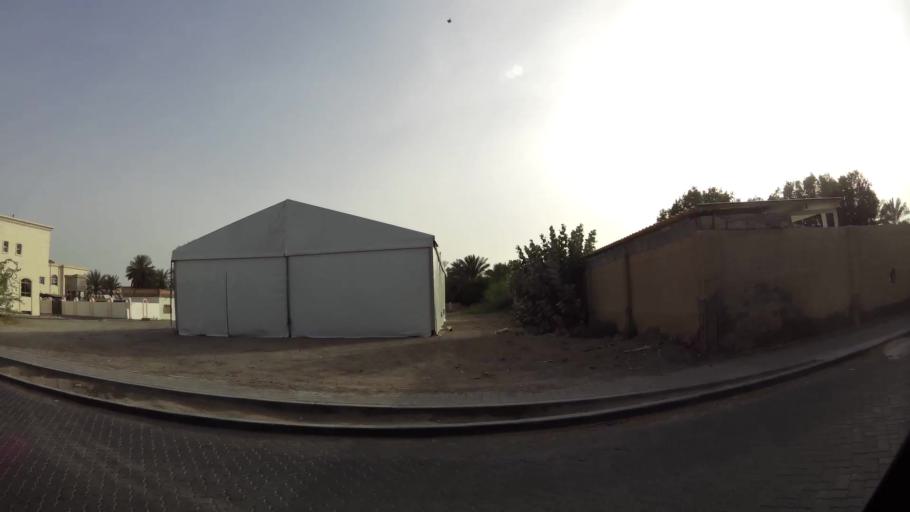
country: AE
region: Abu Dhabi
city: Al Ain
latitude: 24.2243
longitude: 55.7156
